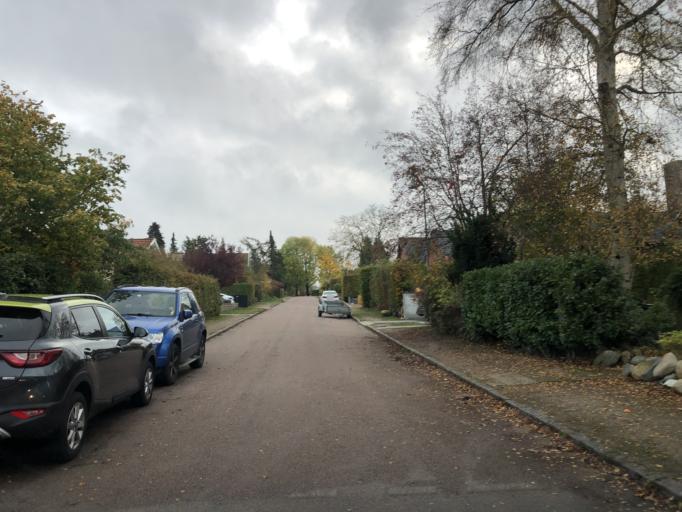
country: DK
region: Capital Region
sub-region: Rudersdal Kommune
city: Holte
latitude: 55.7922
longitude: 12.4696
